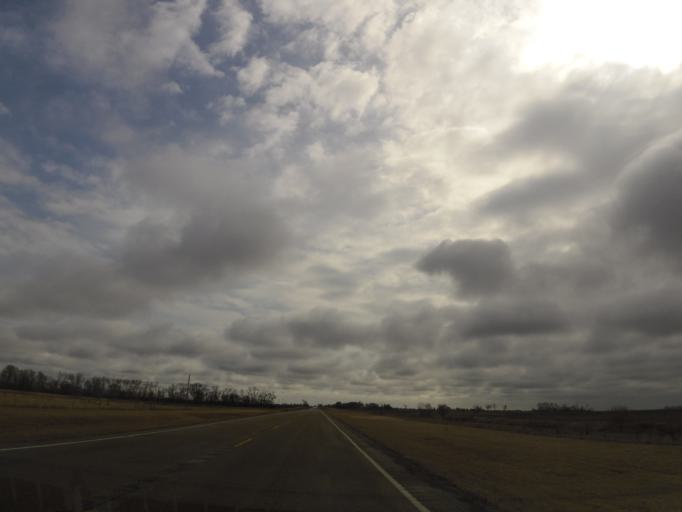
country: US
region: North Dakota
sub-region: Traill County
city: Mayville
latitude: 47.3529
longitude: -97.3008
